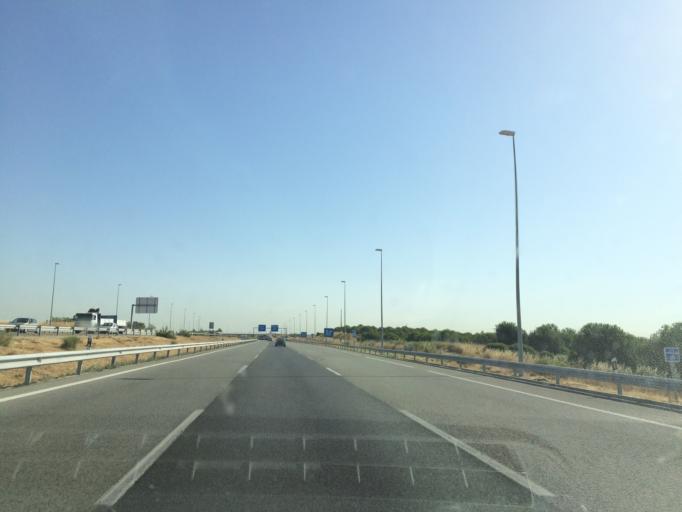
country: ES
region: Madrid
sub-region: Provincia de Madrid
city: Navalcarnero
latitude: 40.2601
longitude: -4.0446
